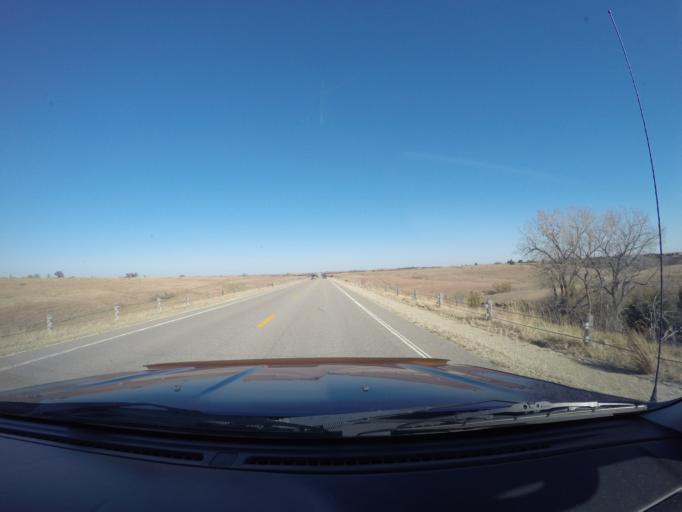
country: US
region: Kansas
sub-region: Riley County
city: Ogden
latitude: 39.3102
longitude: -96.7557
